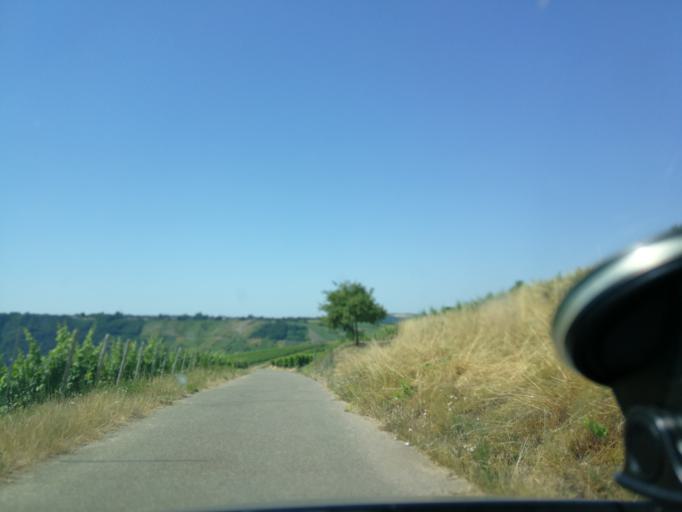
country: DE
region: Rheinland-Pfalz
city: Minheim
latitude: 49.8761
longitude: 6.9366
